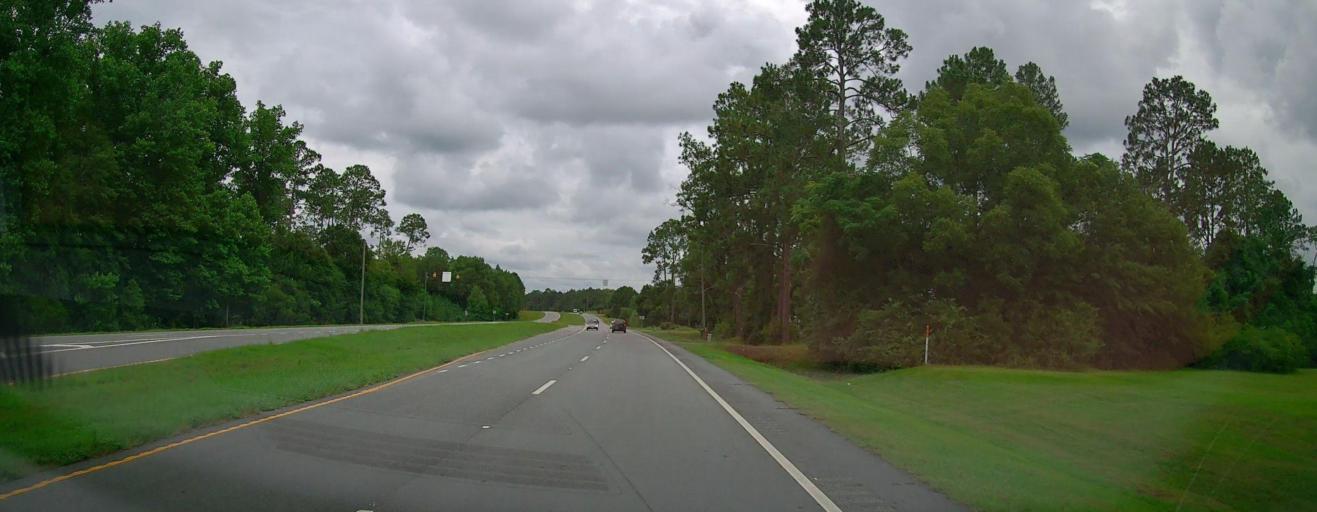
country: US
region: Georgia
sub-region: Telfair County
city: McRae
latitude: 32.0494
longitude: -82.8602
